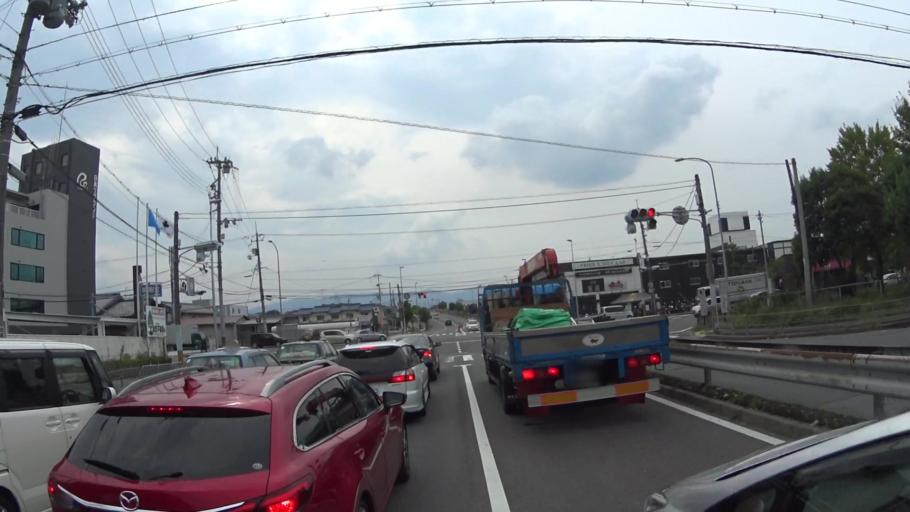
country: JP
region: Kyoto
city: Muko
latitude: 34.9515
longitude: 135.7460
